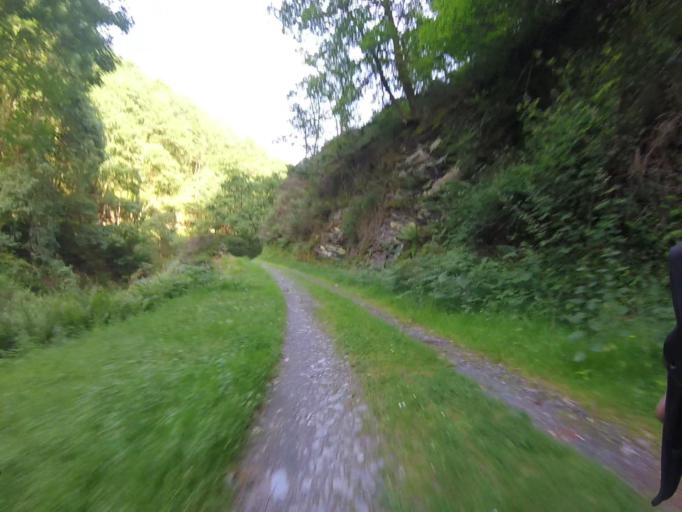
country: ES
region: Navarre
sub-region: Provincia de Navarra
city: Arano
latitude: 43.2371
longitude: -1.8741
